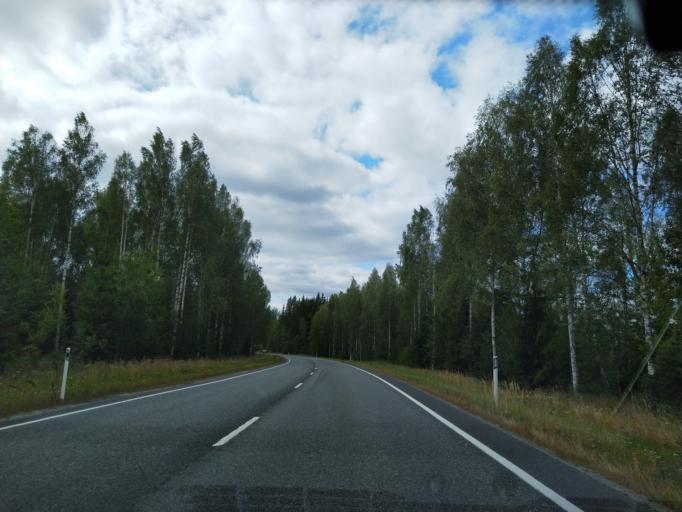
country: FI
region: Haeme
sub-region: Riihimaeki
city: Riihimaeki
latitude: 60.7472
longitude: 24.7056
